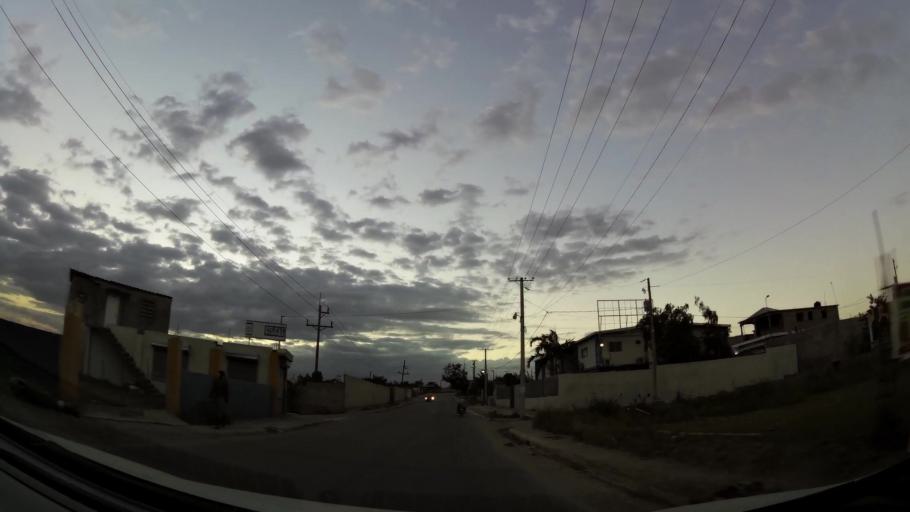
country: DO
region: Nacional
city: La Agustina
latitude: 18.5538
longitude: -69.9461
